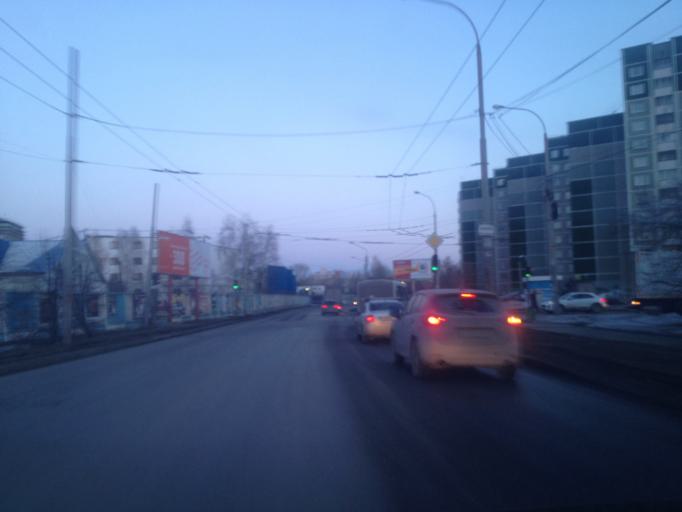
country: RU
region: Sverdlovsk
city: Yekaterinburg
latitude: 56.7941
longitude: 60.6350
